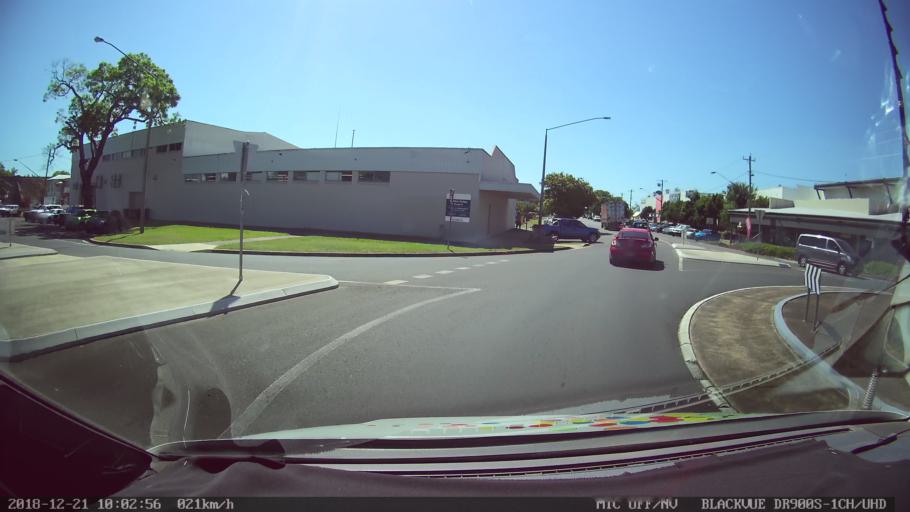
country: AU
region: New South Wales
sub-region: Clarence Valley
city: Grafton
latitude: -29.6901
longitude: 152.9359
